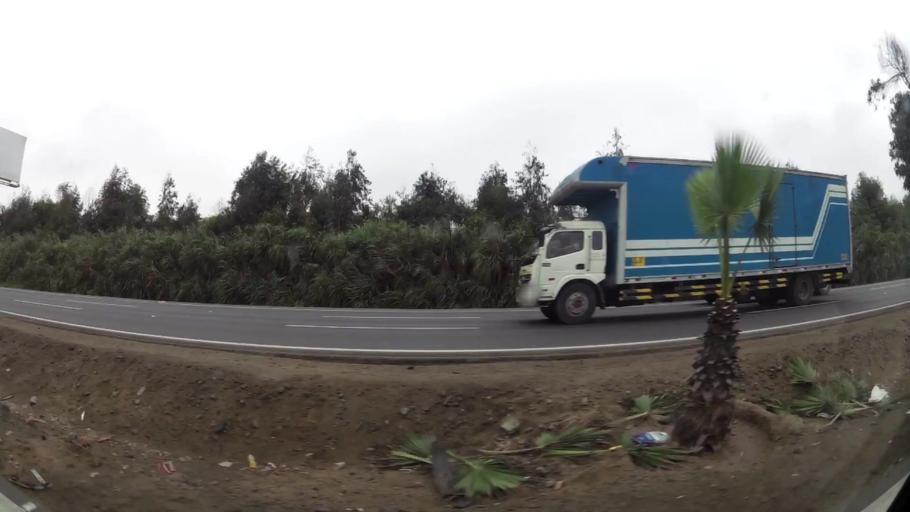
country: PE
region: Lima
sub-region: Lima
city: Punta Hermosa
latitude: -12.2679
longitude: -76.9029
